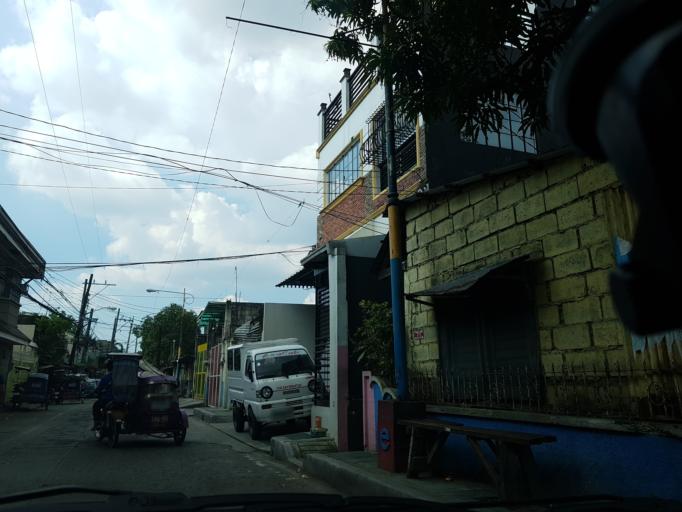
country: PH
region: Calabarzon
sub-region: Province of Rizal
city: Pateros
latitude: 14.5596
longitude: 121.0897
